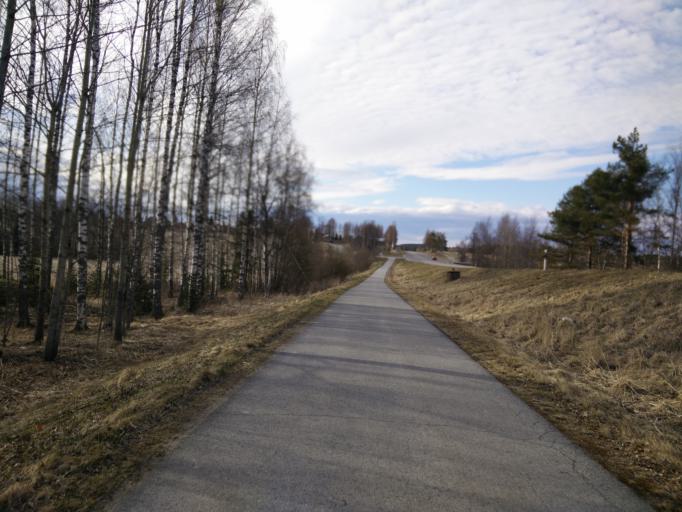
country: FI
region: Pirkanmaa
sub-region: Tampere
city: Orivesi
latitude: 61.7065
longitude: 24.3357
